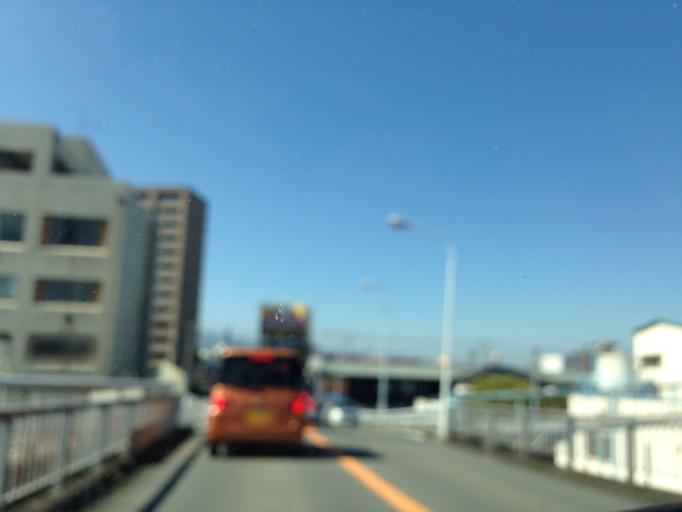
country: JP
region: Shizuoka
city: Numazu
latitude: 35.0992
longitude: 138.8705
